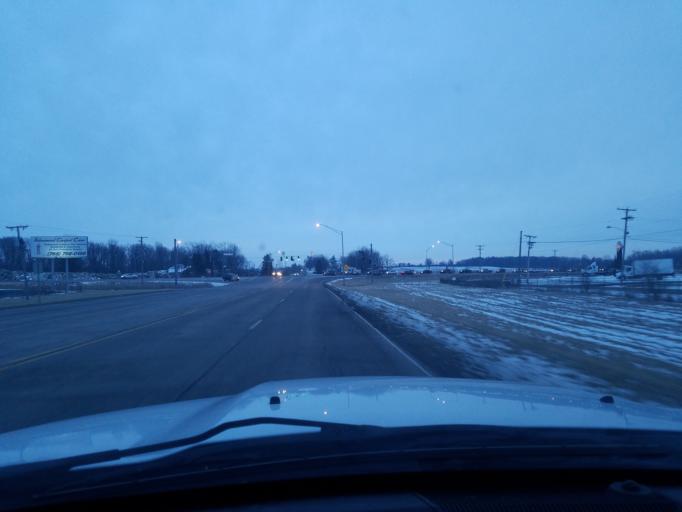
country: US
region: Indiana
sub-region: Delaware County
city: Muncie
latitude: 40.2191
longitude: -85.3430
